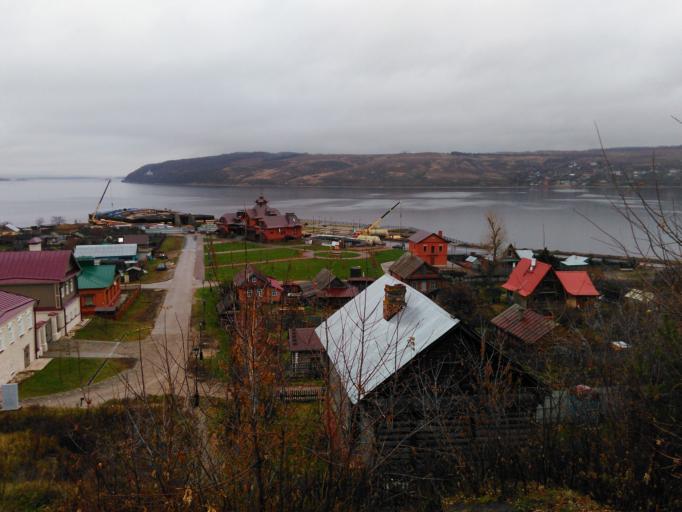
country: RU
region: Tatarstan
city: Sviyazhsk
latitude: 55.7733
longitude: 48.6637
